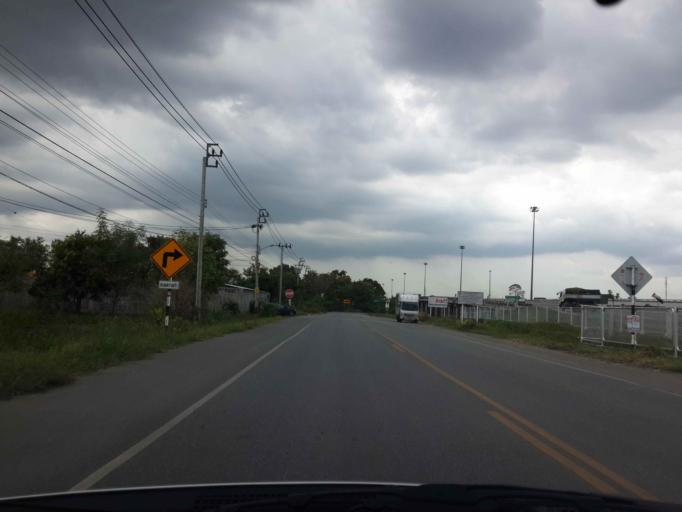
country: TH
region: Bangkok
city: Sai Mai
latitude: 13.8965
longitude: 100.6933
